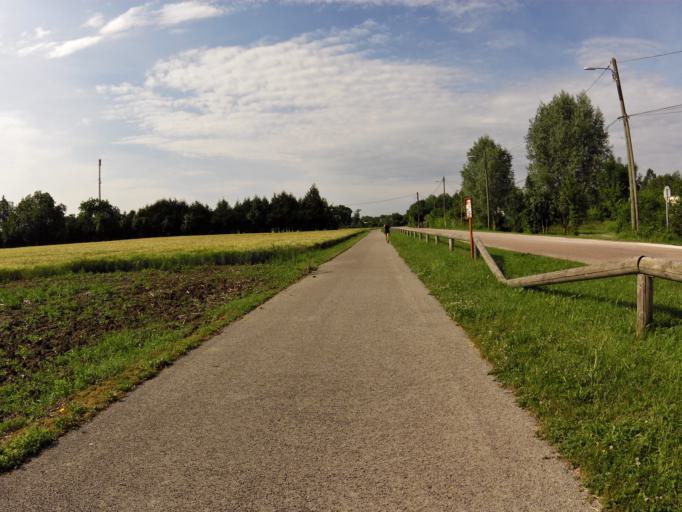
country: FR
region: Champagne-Ardenne
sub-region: Departement de l'Aube
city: Saint-Julien-les-Villas
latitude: 48.2745
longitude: 4.1116
